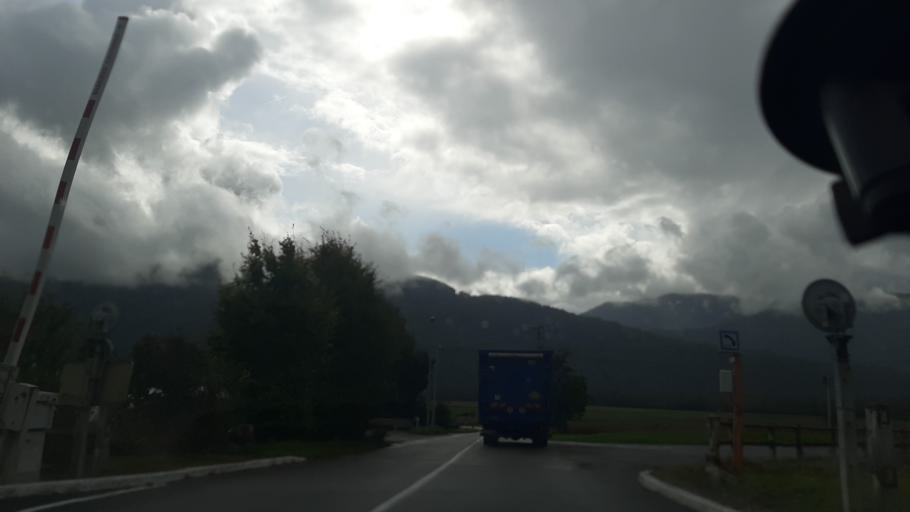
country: FR
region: Rhone-Alpes
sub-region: Departement de la Savoie
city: Gresy-sur-Isere
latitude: 45.5946
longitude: 6.2605
